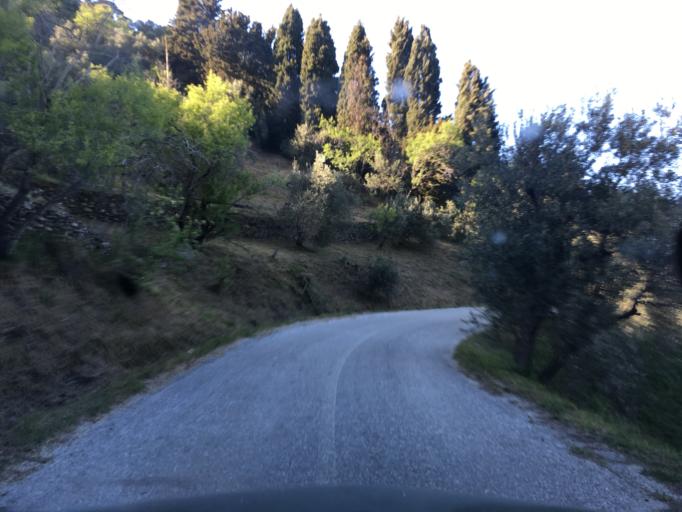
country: GR
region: Thessaly
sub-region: Nomos Magnisias
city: Skopelos
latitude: 39.1817
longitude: 23.6190
